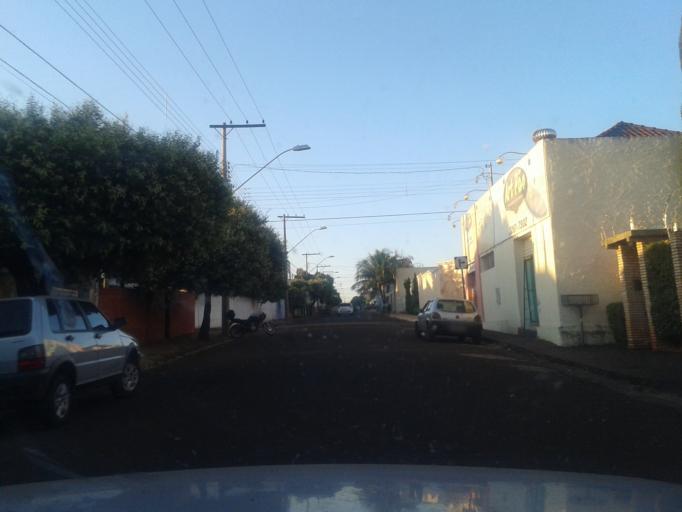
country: BR
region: Minas Gerais
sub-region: Ituiutaba
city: Ituiutaba
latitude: -18.9789
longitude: -49.4651
